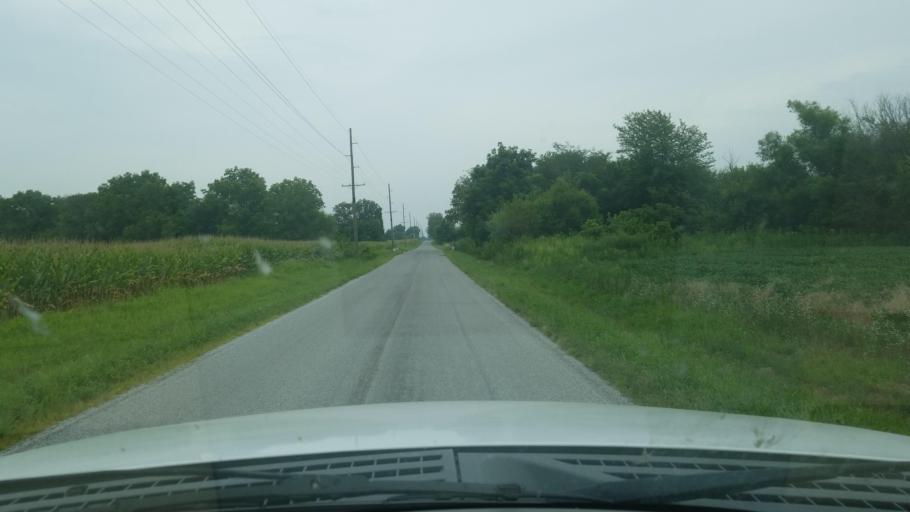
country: US
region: Illinois
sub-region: Saline County
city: Eldorado
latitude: 37.8630
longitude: -88.5199
